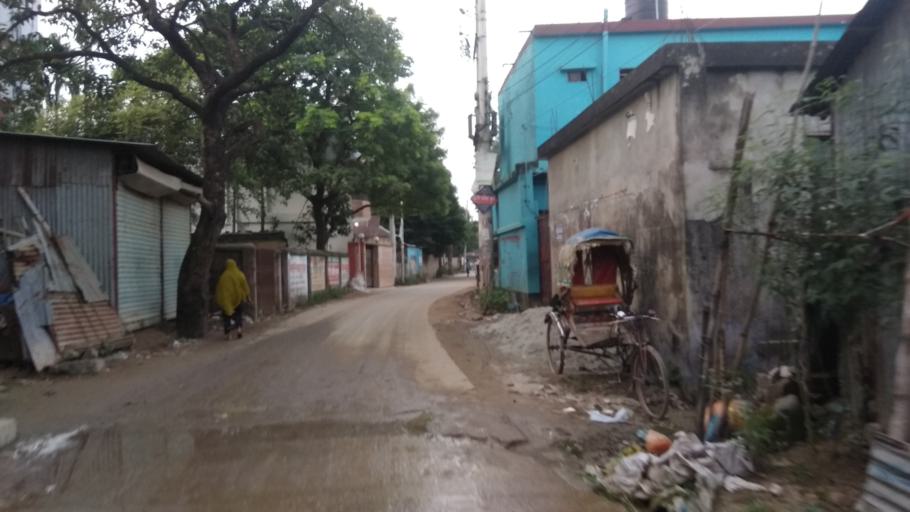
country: BD
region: Dhaka
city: Tungi
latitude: 23.8508
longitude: 90.4251
